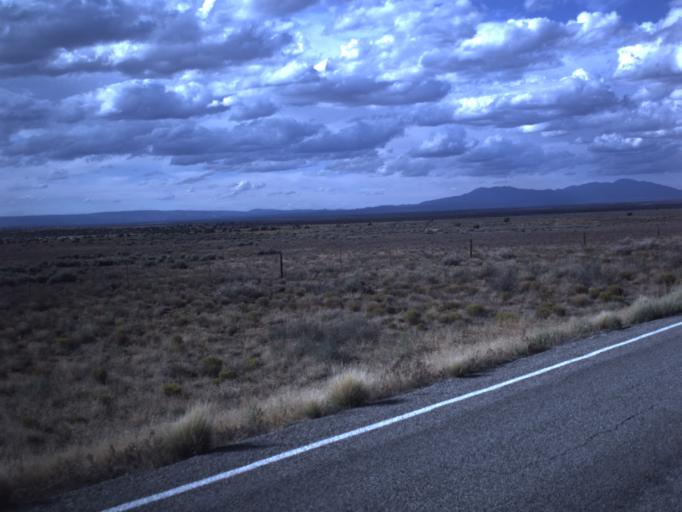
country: US
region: Utah
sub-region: San Juan County
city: Blanding
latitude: 37.3636
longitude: -109.3447
